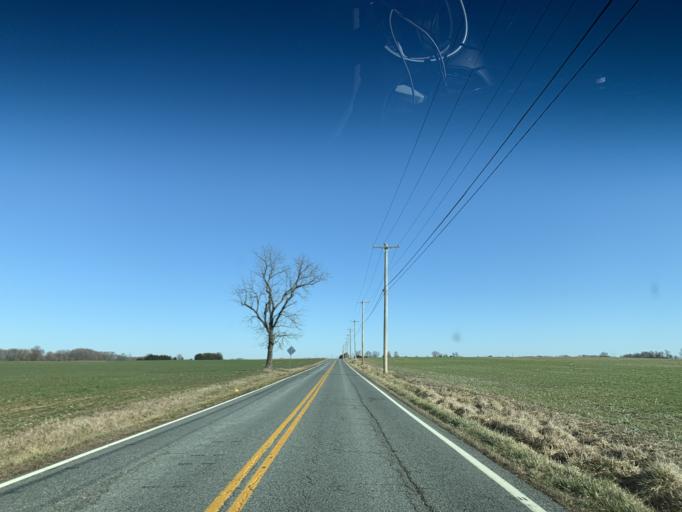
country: US
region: Maryland
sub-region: Cecil County
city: Elkton
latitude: 39.4891
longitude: -75.8690
